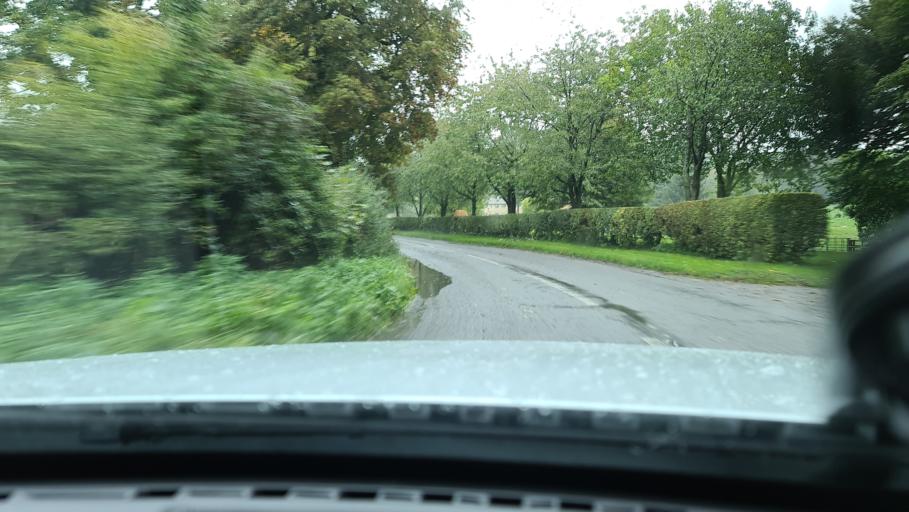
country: GB
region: England
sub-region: Oxfordshire
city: Woodstock
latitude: 51.8898
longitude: -1.3791
